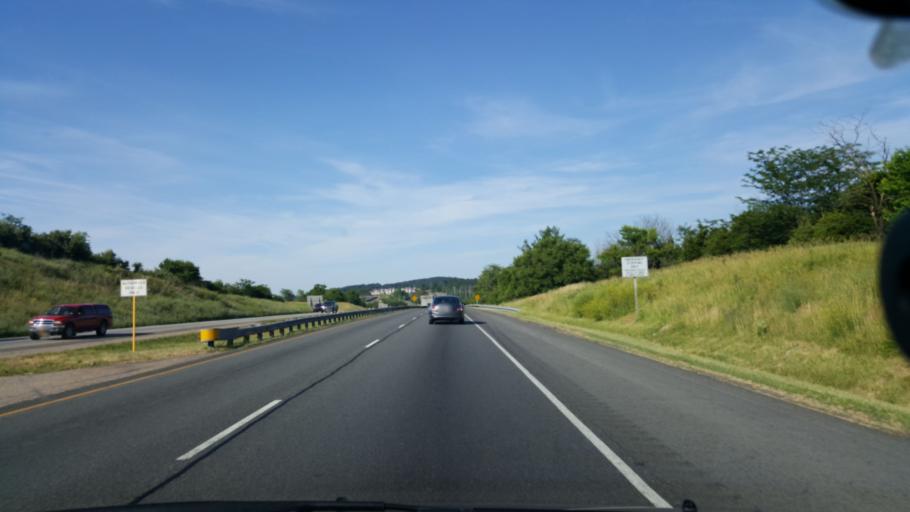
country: US
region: Virginia
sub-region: Rockingham County
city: Dayton
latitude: 38.4094
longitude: -78.8970
